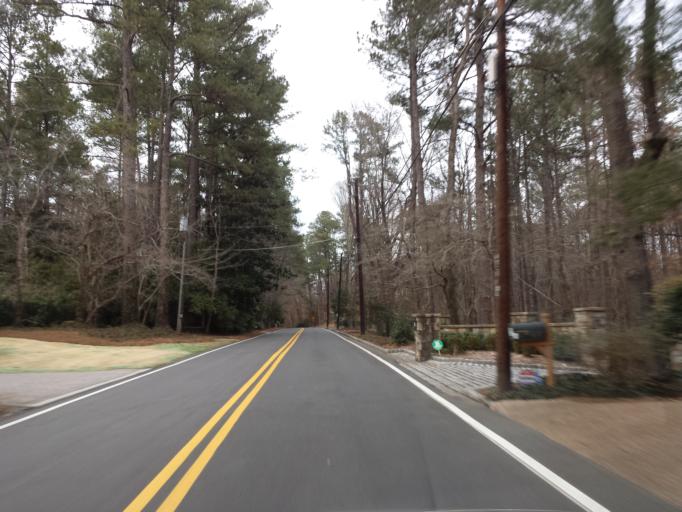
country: US
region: Georgia
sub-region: Cobb County
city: Vinings
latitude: 33.8792
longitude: -84.4326
